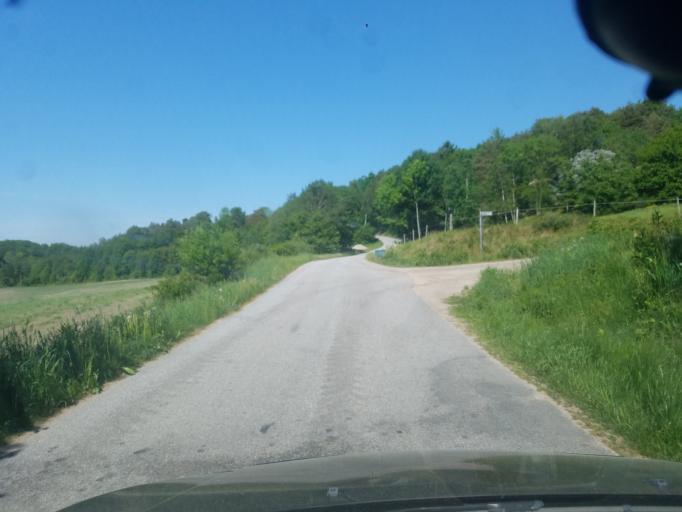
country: SE
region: Vaestra Goetaland
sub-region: Orust
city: Henan
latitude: 58.2722
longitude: 11.5721
